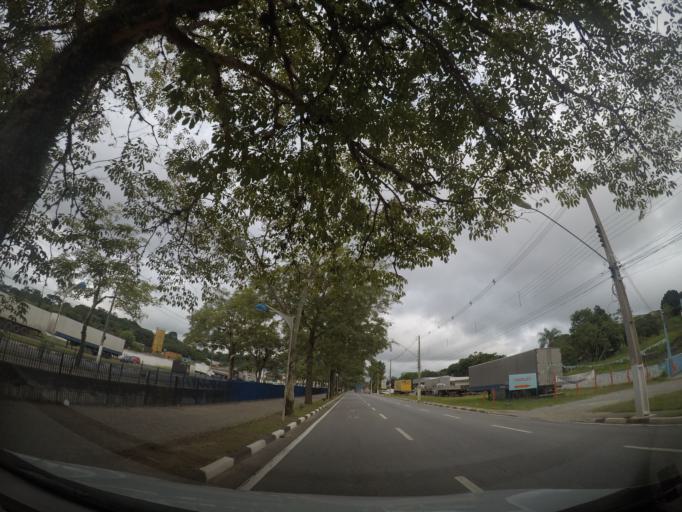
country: BR
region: Sao Paulo
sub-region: Aruja
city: Aruja
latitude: -23.3968
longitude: -46.3328
